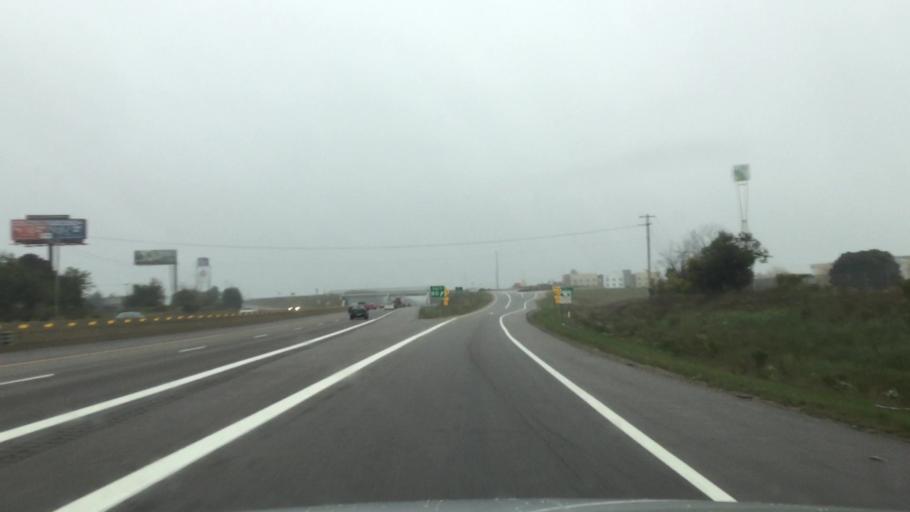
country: US
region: Michigan
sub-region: Kalamazoo County
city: Eastwood
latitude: 42.2561
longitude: -85.5352
